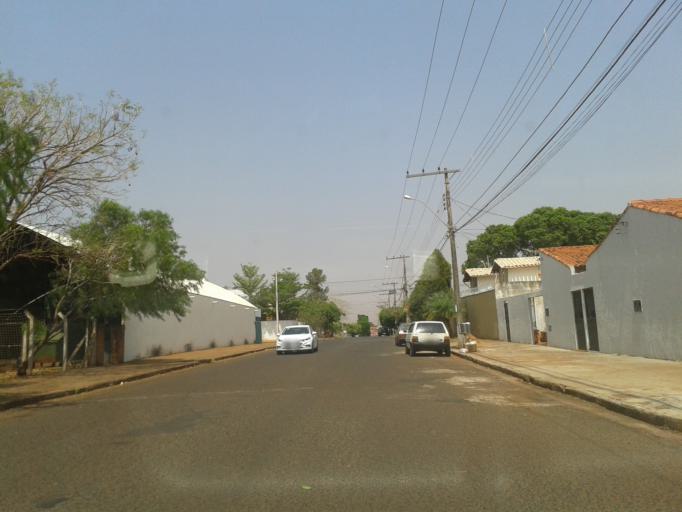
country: BR
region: Minas Gerais
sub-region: Ituiutaba
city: Ituiutaba
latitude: -18.9685
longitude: -49.4460
